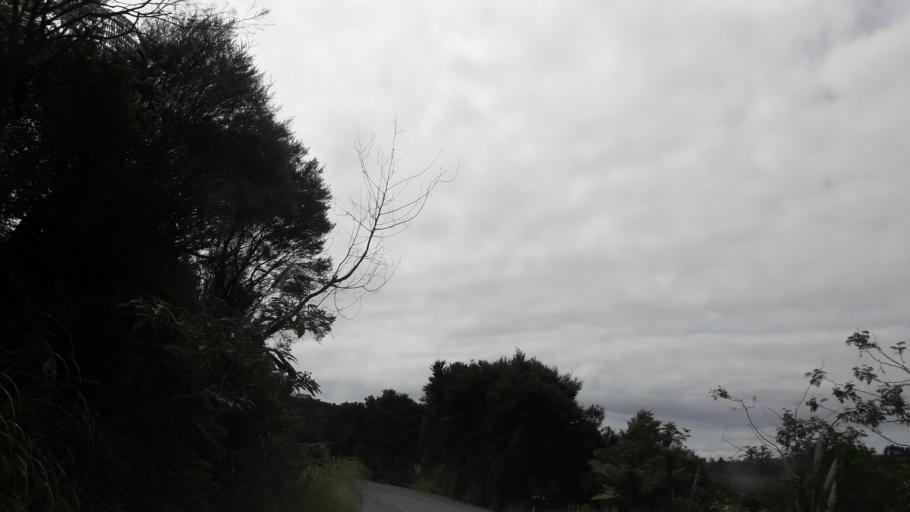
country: NZ
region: Northland
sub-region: Far North District
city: Taipa
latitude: -35.0220
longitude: 173.5508
